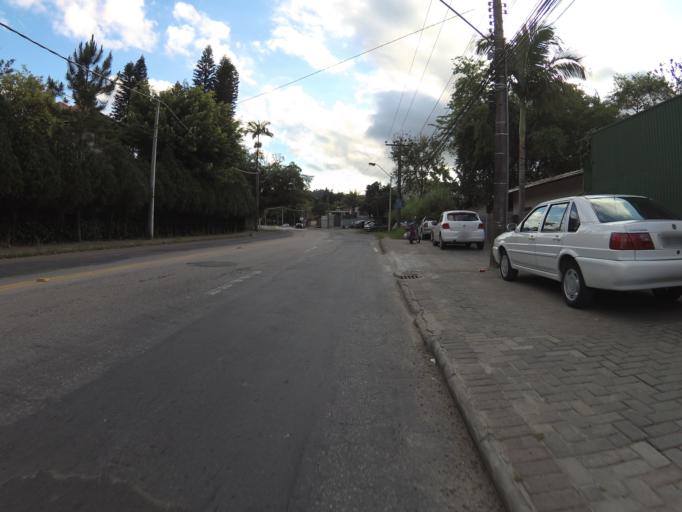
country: BR
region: Santa Catarina
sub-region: Blumenau
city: Blumenau
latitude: -26.8852
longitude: -49.1129
